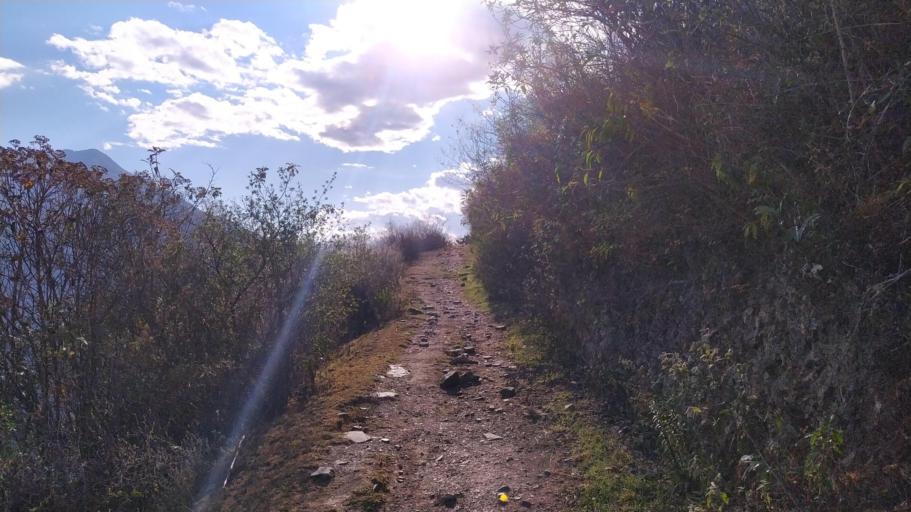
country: PE
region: Apurimac
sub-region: Provincia de Abancay
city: Cachora
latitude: -13.4019
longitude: -72.8565
